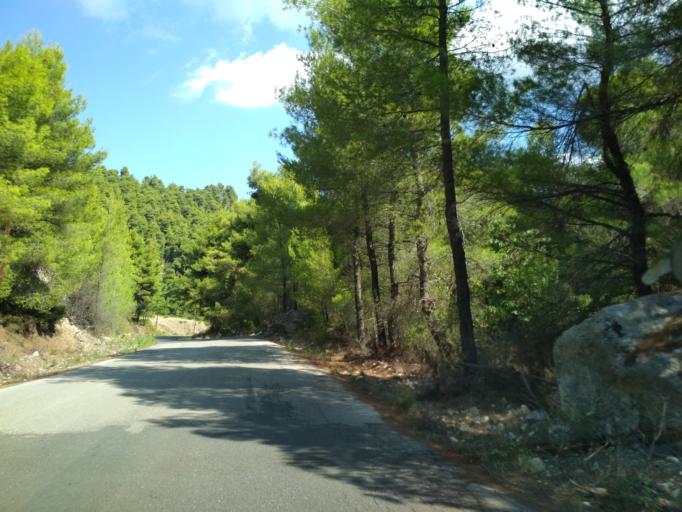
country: GR
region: Central Greece
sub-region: Nomos Evvoias
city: Roviai
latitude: 38.8211
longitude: 23.2775
